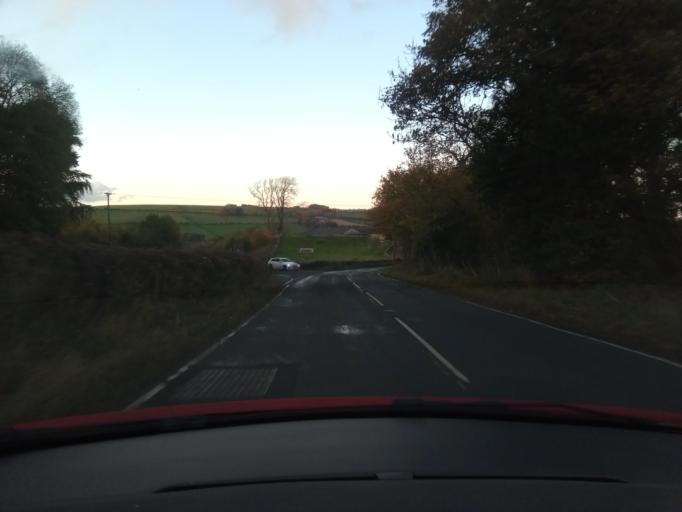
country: GB
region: England
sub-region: Northumberland
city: Bardon Mill
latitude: 54.9664
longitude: -2.2428
